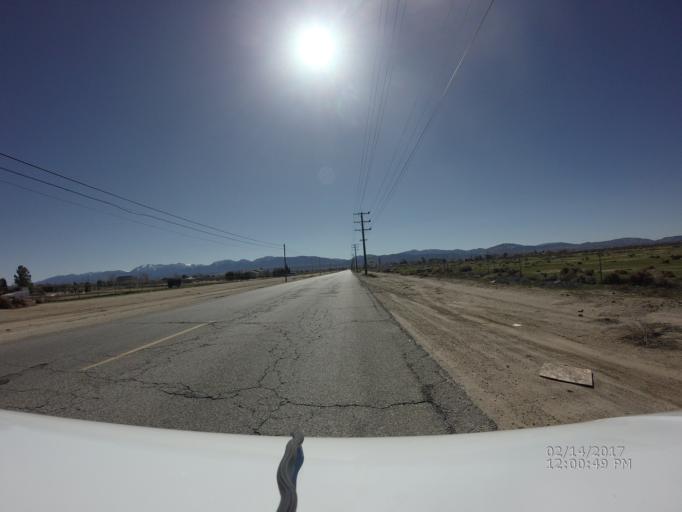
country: US
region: California
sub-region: Los Angeles County
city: Littlerock
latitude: 34.5869
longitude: -117.9692
